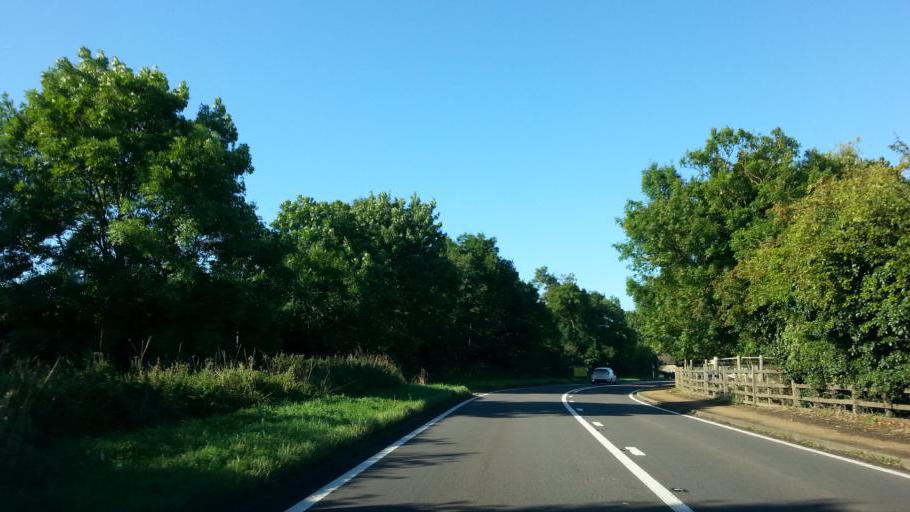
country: GB
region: England
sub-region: District of Rutland
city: Tinwell
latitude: 52.6282
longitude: -0.4983
